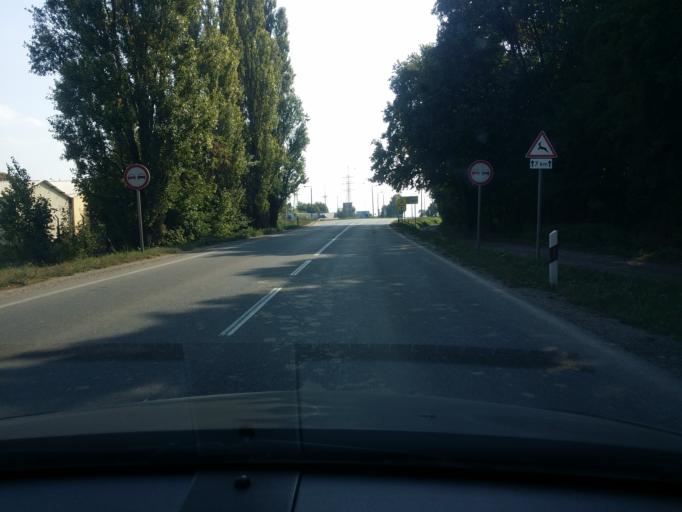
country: HU
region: Fejer
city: Dunaujvaros
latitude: 46.9279
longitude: 18.9299
